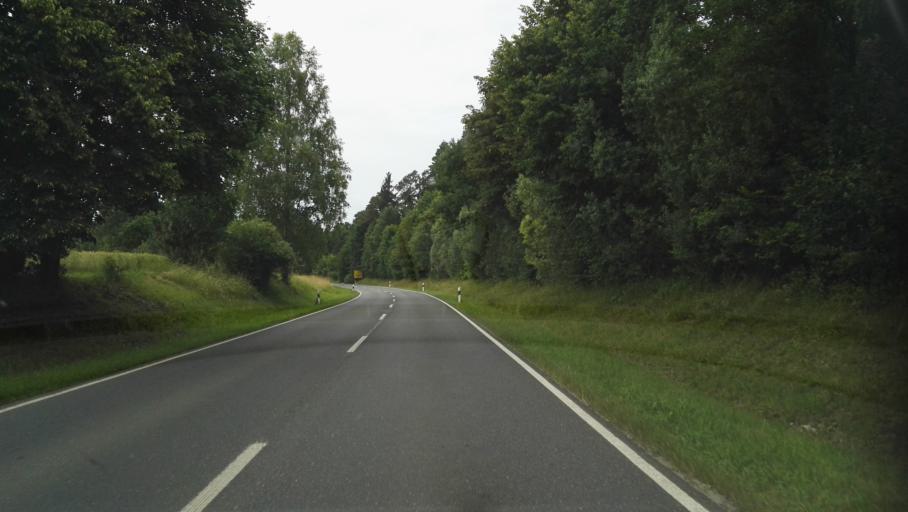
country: DE
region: Bavaria
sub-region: Upper Franconia
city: Plankenfels
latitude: 49.9072
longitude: 11.3251
